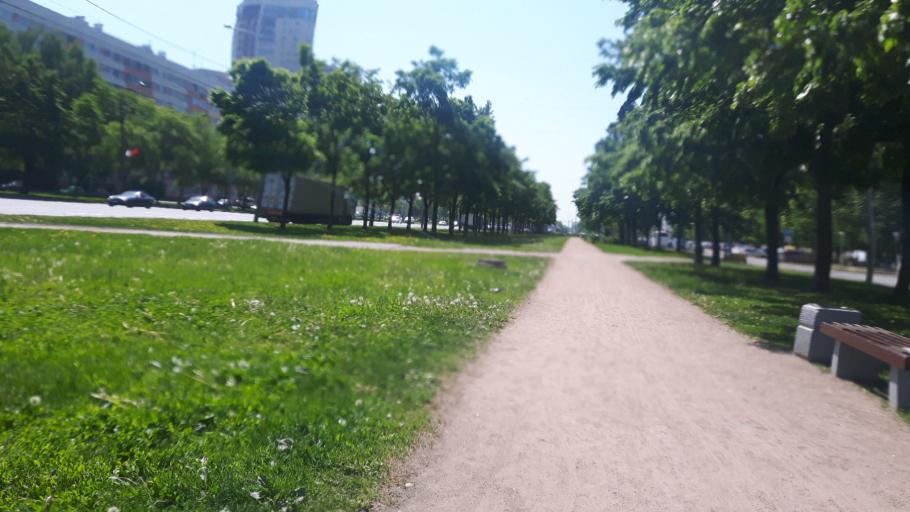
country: RU
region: St.-Petersburg
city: Dachnoye
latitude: 59.8555
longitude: 30.2260
